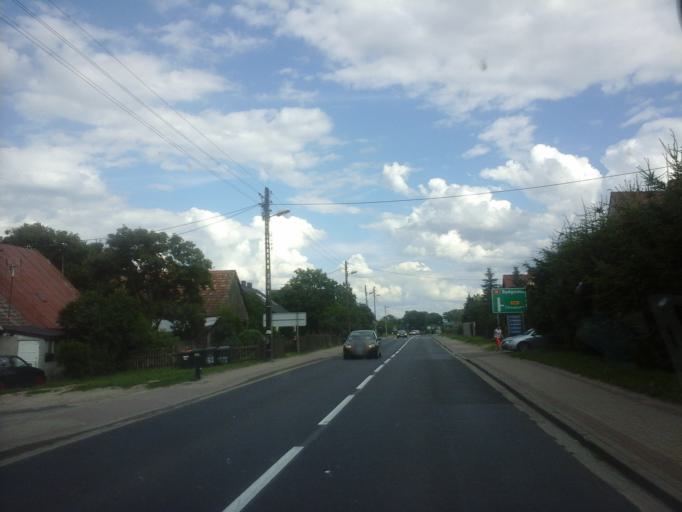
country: PL
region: West Pomeranian Voivodeship
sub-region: Powiat stargardzki
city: Suchan
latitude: 53.2792
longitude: 15.3275
